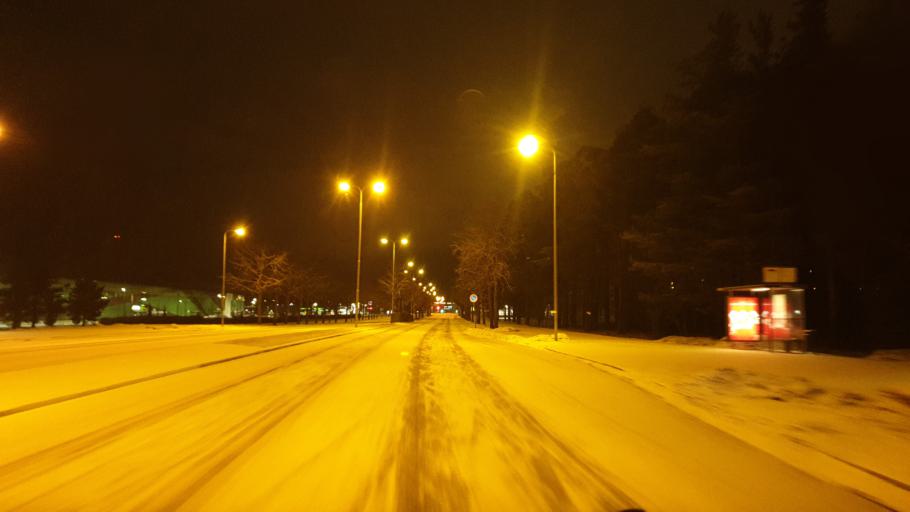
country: FI
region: Northern Ostrobothnia
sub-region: Oulu
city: Oulu
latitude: 64.9925
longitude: 25.4653
